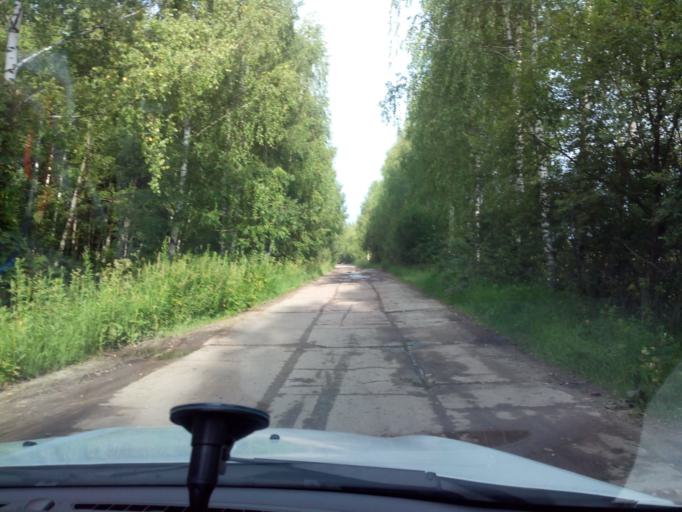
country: RU
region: Vladimir
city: Petushki
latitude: 56.0362
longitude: 39.5000
